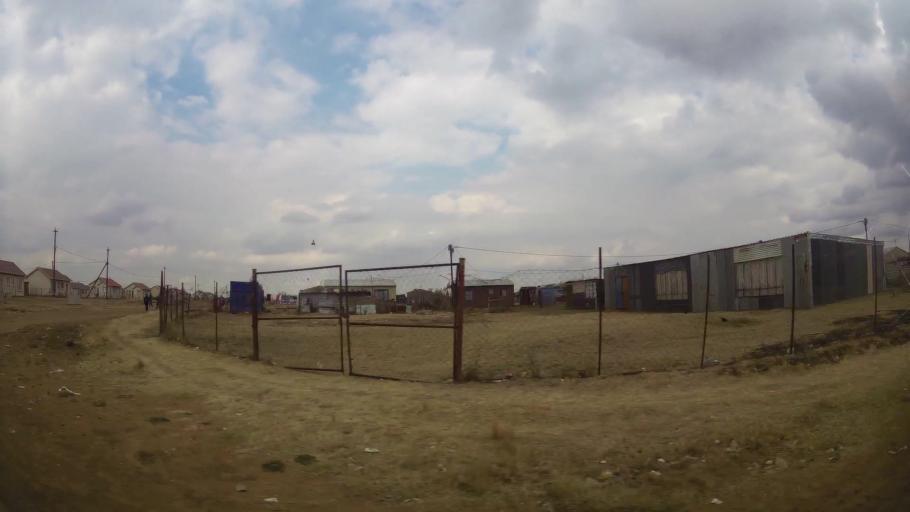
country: ZA
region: Orange Free State
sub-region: Fezile Dabi District Municipality
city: Sasolburg
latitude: -26.8592
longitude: 27.8668
